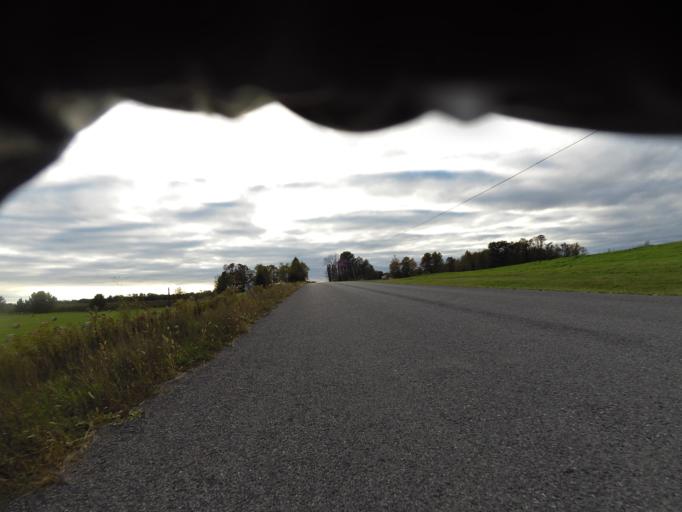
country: CA
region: Ontario
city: Cobourg
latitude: 43.9806
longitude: -77.9883
